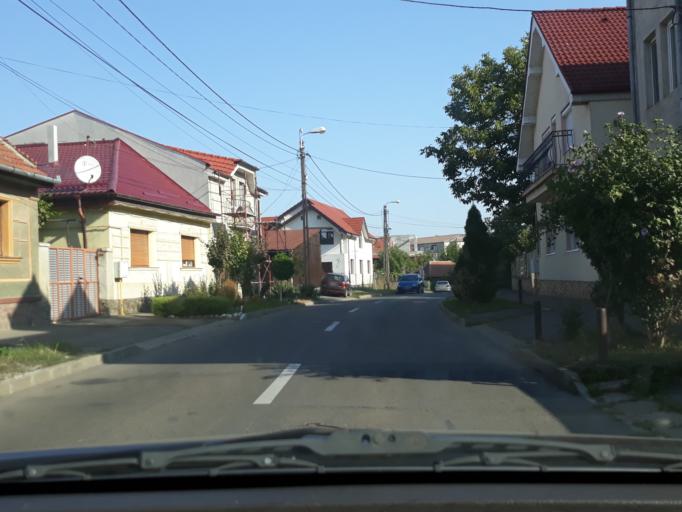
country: RO
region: Bihor
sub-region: Comuna Biharea
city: Oradea
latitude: 47.0356
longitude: 21.9397
